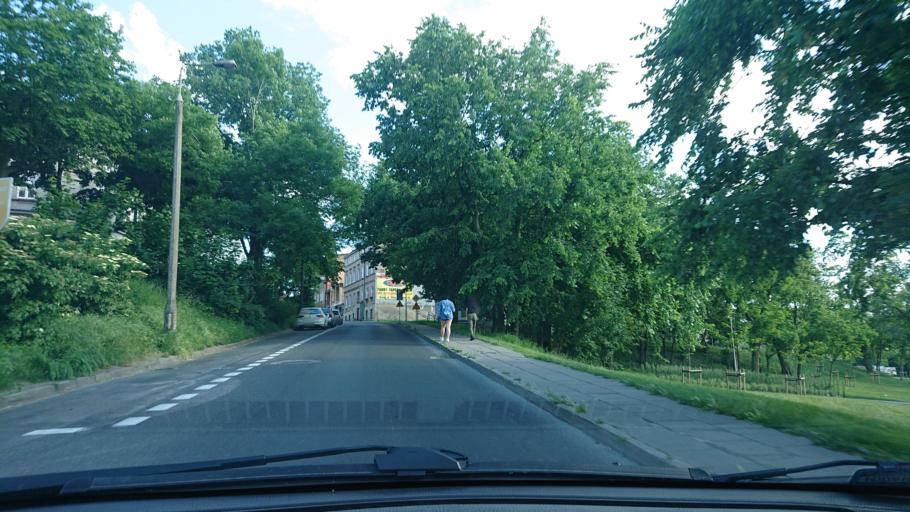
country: PL
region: Greater Poland Voivodeship
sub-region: Powiat gnieznienski
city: Gniezno
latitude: 52.5330
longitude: 17.5917
